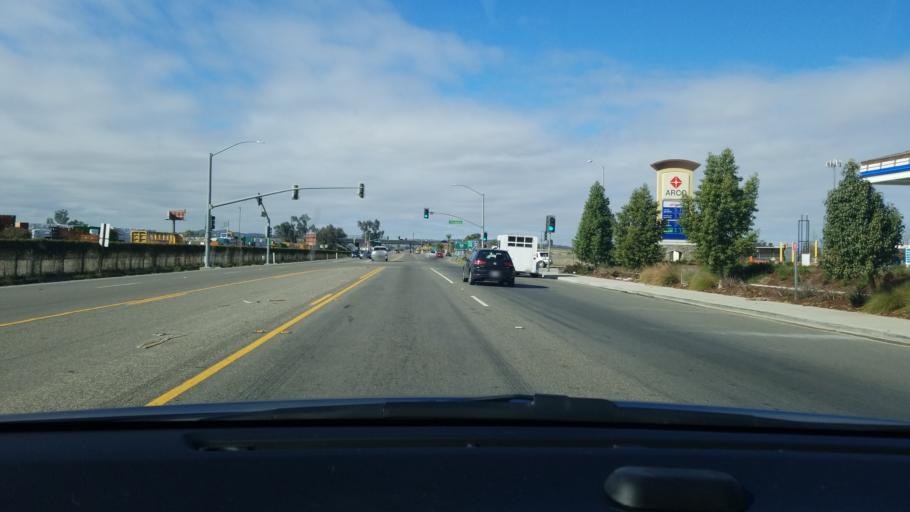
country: US
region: California
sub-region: Riverside County
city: Romoland
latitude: 33.7516
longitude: -117.1848
